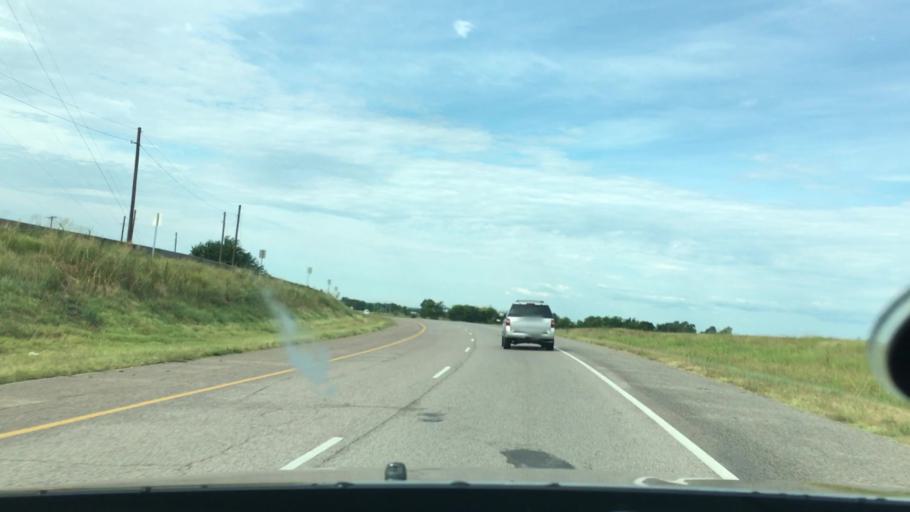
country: US
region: Oklahoma
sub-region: Pontotoc County
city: Ada
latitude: 34.6851
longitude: -96.7623
